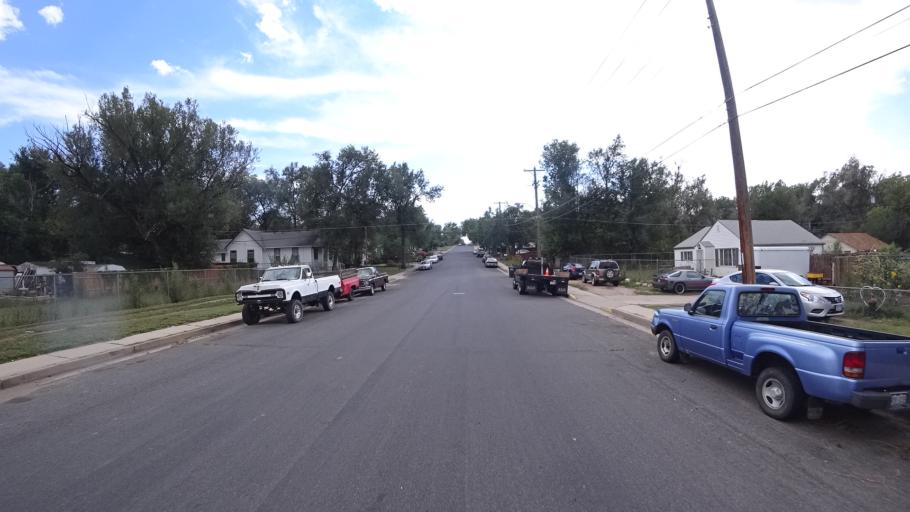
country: US
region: Colorado
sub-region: El Paso County
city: Colorado Springs
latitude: 38.8303
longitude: -104.8082
